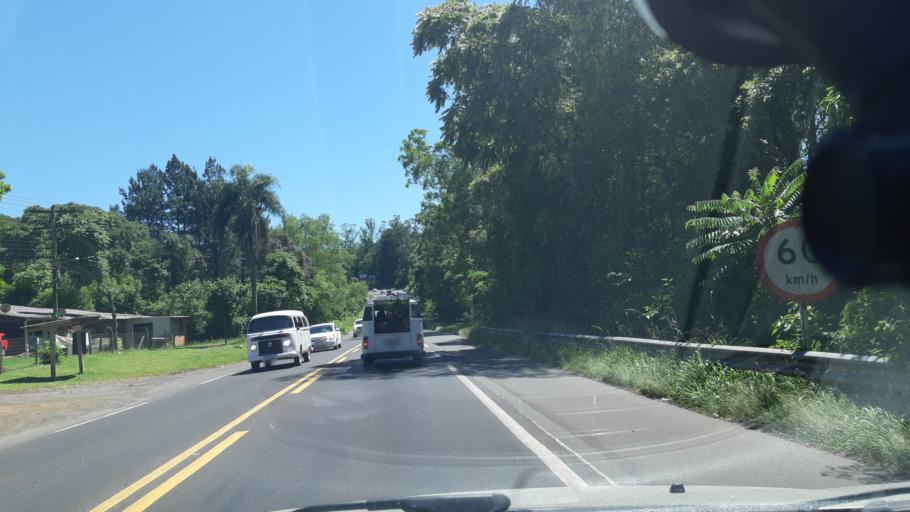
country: BR
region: Rio Grande do Sul
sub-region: Estancia Velha
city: Estancia Velha
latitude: -29.6406
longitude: -51.1424
